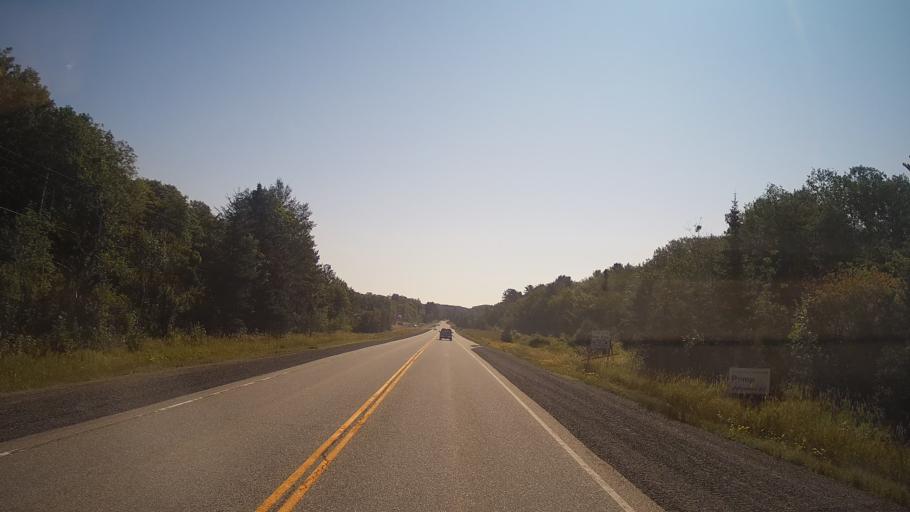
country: CA
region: Ontario
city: Elliot Lake
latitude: 46.2051
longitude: -82.4282
